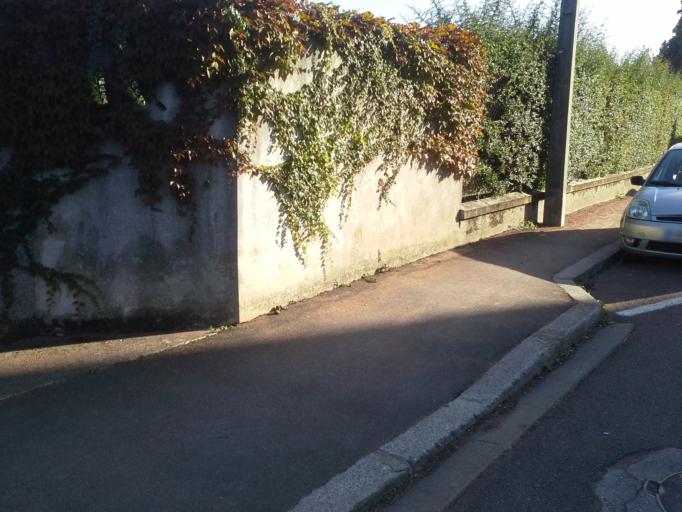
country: FR
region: Centre
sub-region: Departement d'Indre-et-Loire
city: La Riche
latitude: 47.3896
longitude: 0.6661
